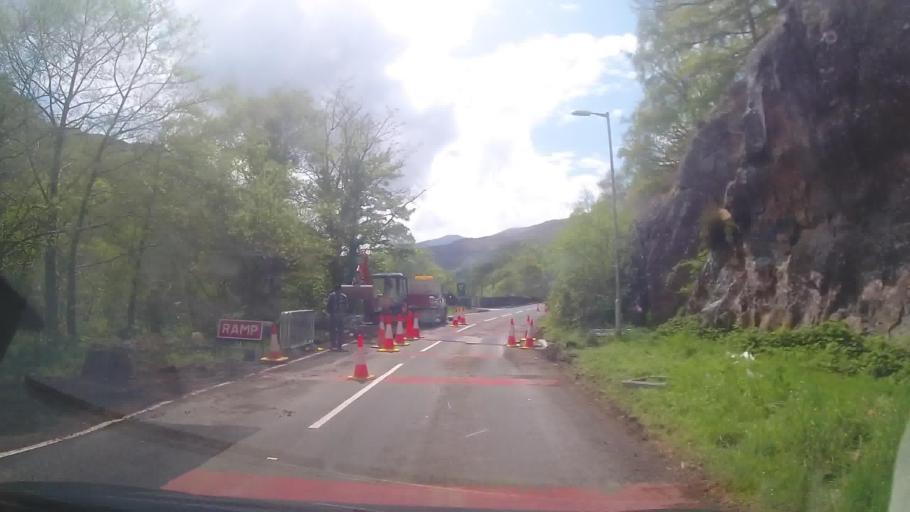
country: GB
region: Wales
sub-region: Gwynedd
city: Penrhyndeudraeth
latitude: 53.0156
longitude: -4.0961
